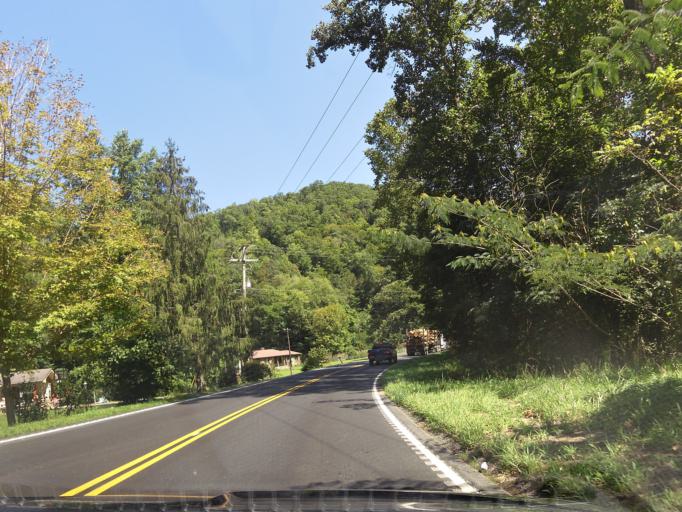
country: US
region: Kentucky
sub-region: Leslie County
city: Hyden
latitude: 37.1459
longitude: -83.4270
